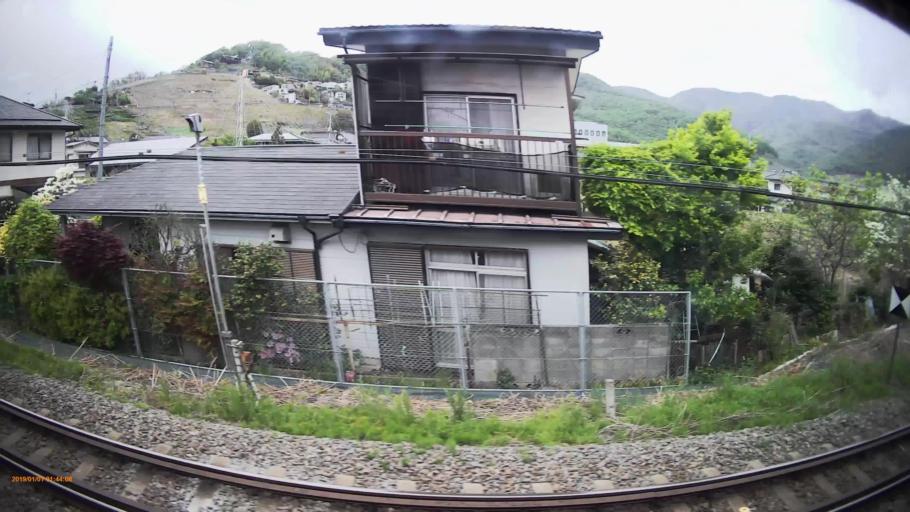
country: JP
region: Yamanashi
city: Kofu-shi
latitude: 35.6616
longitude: 138.5821
